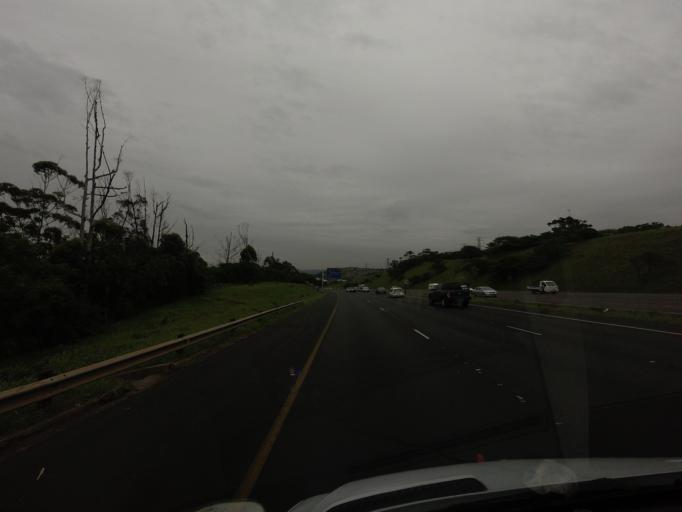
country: ZA
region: KwaZulu-Natal
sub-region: eThekwini Metropolitan Municipality
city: Berea
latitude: -29.7504
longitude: 31.0267
